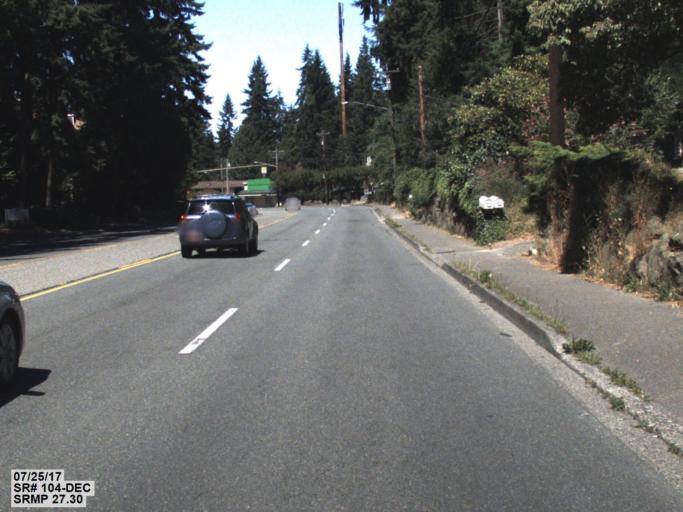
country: US
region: Washington
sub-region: Snohomish County
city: Esperance
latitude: 47.7864
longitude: -122.3536
